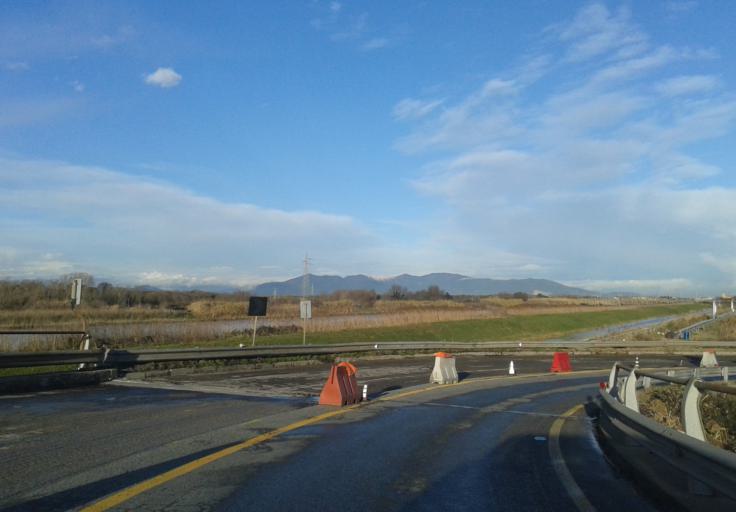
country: IT
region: Tuscany
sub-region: Provincia di Livorno
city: Livorno
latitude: 43.5892
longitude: 10.3222
